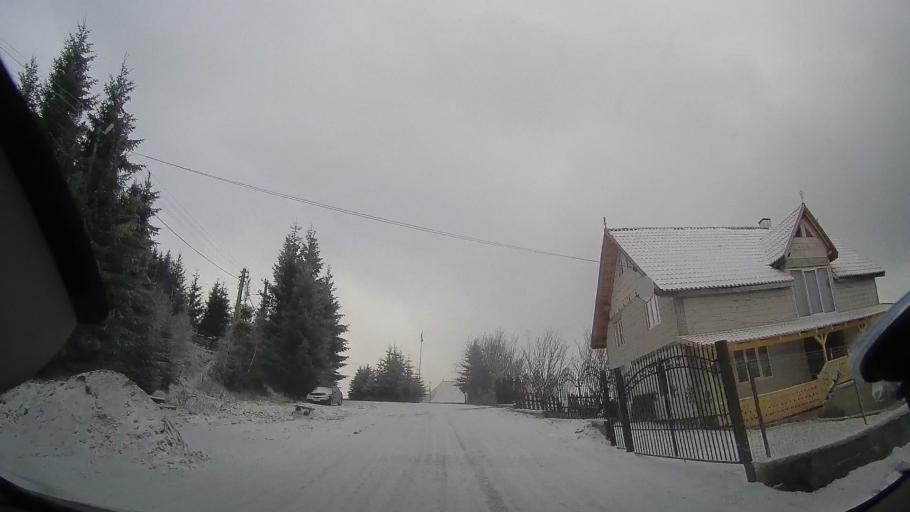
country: RO
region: Cluj
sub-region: Comuna Marisel
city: Marisel
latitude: 46.6627
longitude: 23.1278
